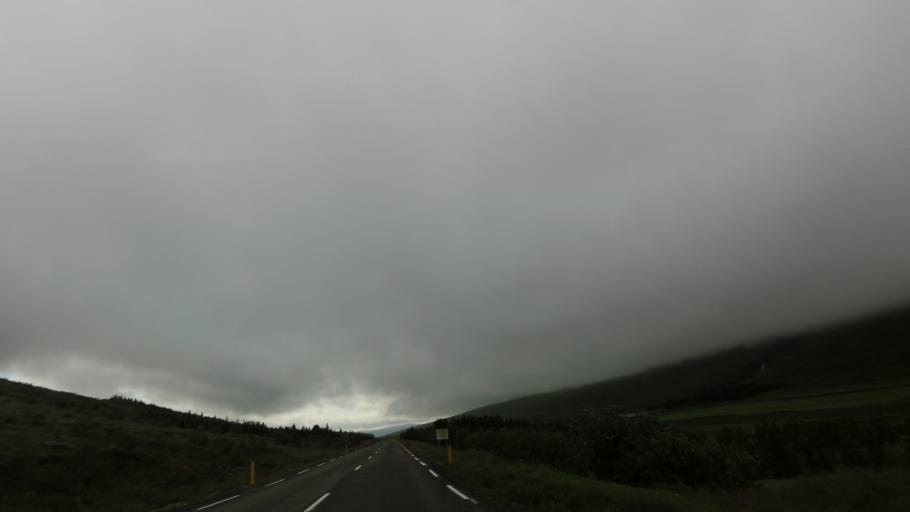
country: IS
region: Northeast
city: Laugar
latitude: 65.7894
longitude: -17.5769
